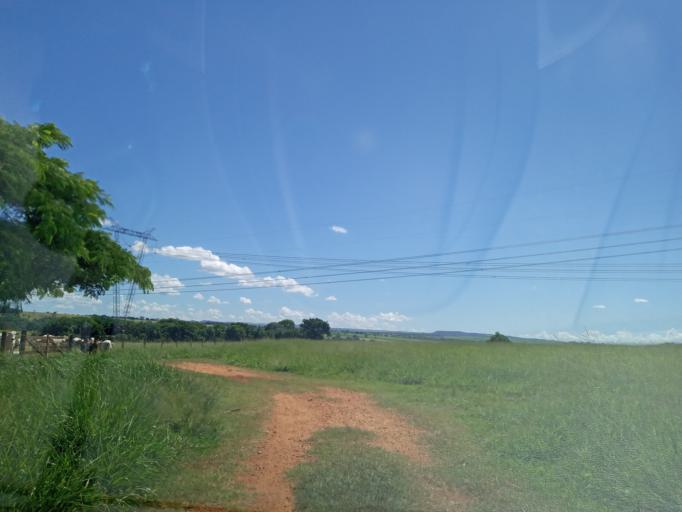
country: BR
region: Goias
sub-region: Itumbiara
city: Itumbiara
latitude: -18.3968
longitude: -49.1247
